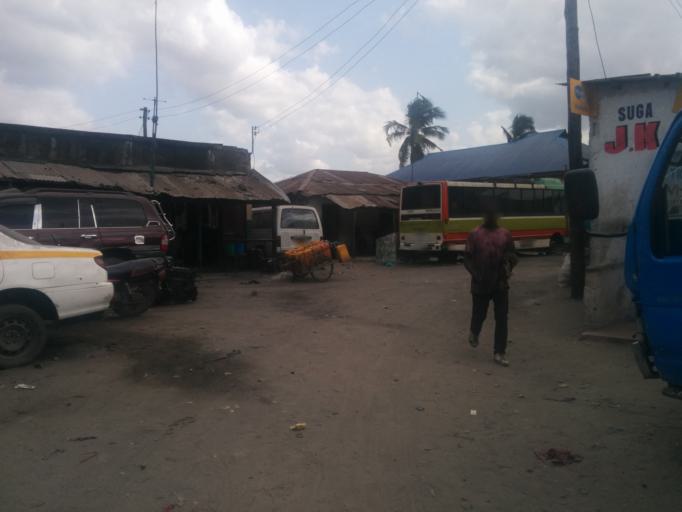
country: TZ
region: Dar es Salaam
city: Magomeni
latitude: -6.7982
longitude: 39.2375
